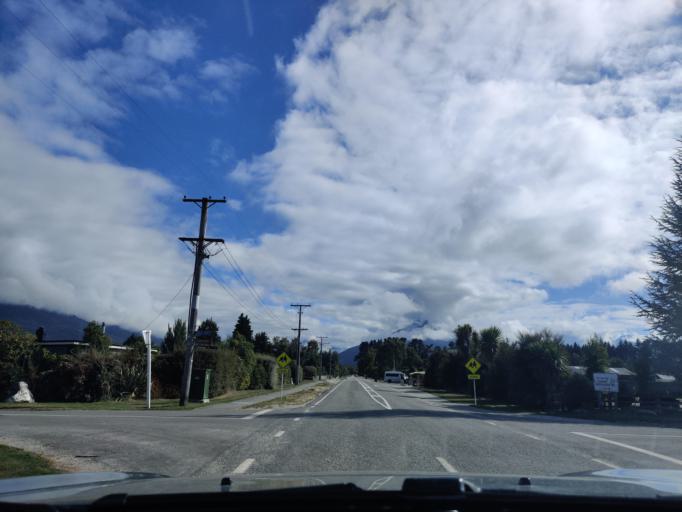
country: NZ
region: Otago
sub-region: Queenstown-Lakes District
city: Queenstown
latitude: -44.8518
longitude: 168.3888
